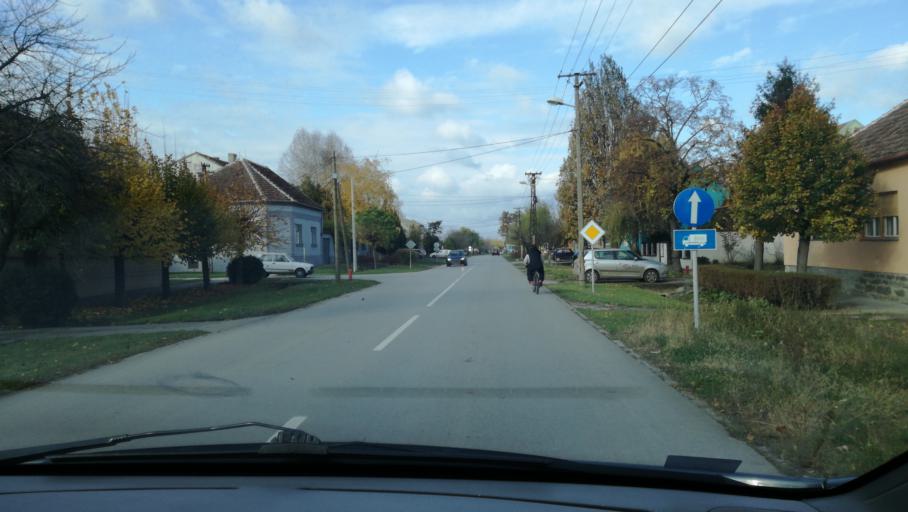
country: RS
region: Autonomna Pokrajina Vojvodina
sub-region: Severnobanatski Okrug
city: Kikinda
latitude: 45.8339
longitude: 20.4593
